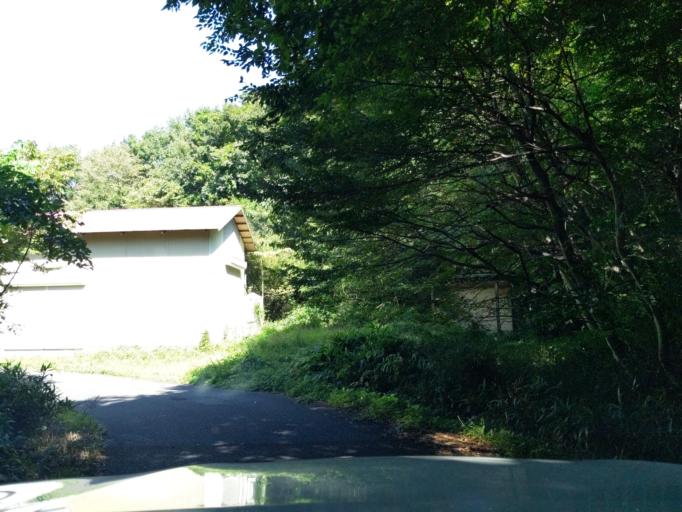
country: JP
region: Fukushima
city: Koriyama
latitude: 37.3977
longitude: 140.2390
